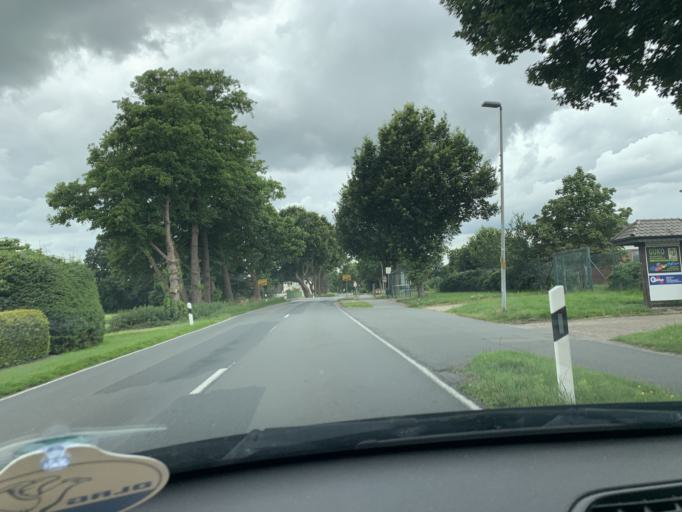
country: DE
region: Lower Saxony
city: Edewecht
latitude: 53.1179
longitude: 7.9617
